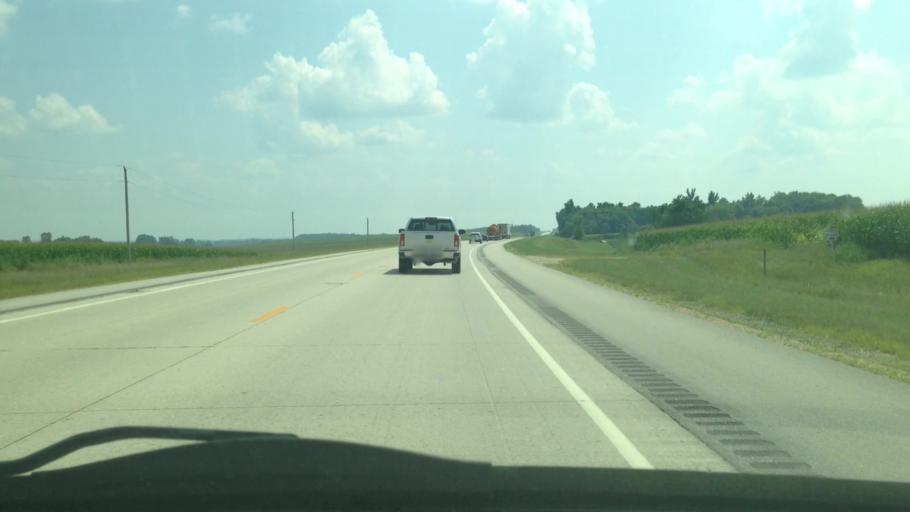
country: US
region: Minnesota
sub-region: Fillmore County
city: Spring Valley
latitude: 43.5393
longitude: -92.3695
